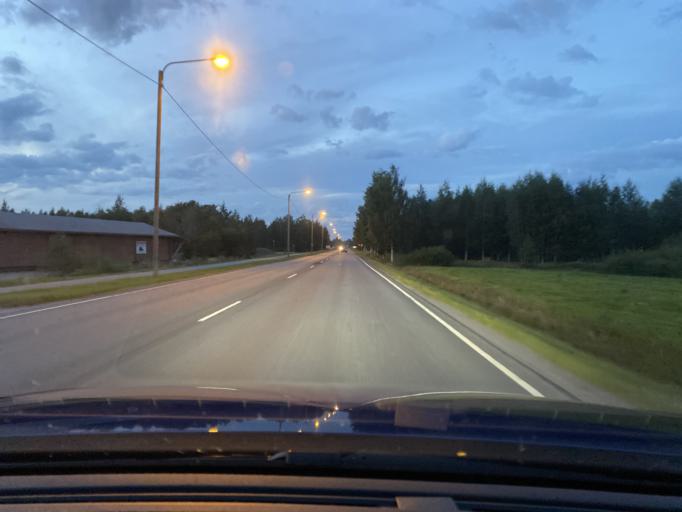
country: FI
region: Southern Ostrobothnia
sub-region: Suupohja
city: Kauhajoki
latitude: 62.4494
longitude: 22.2173
